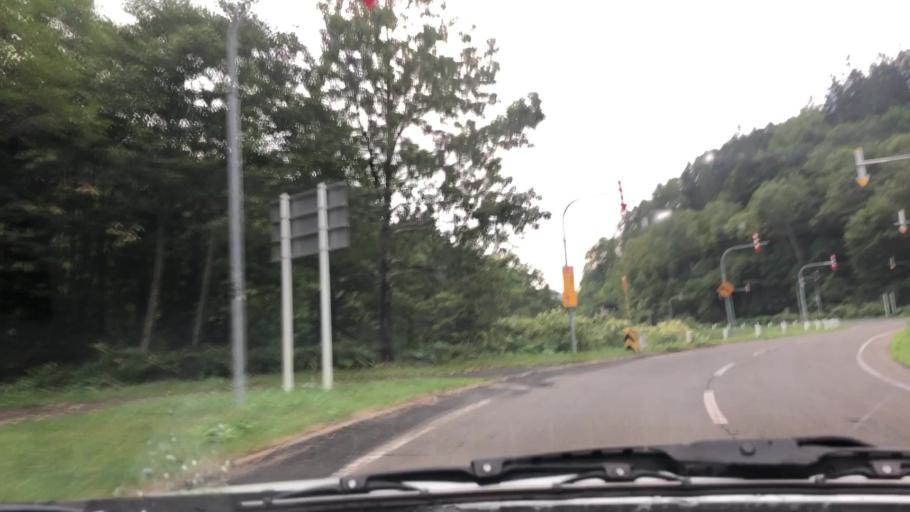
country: JP
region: Hokkaido
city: Shimo-furano
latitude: 42.9330
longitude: 142.3740
